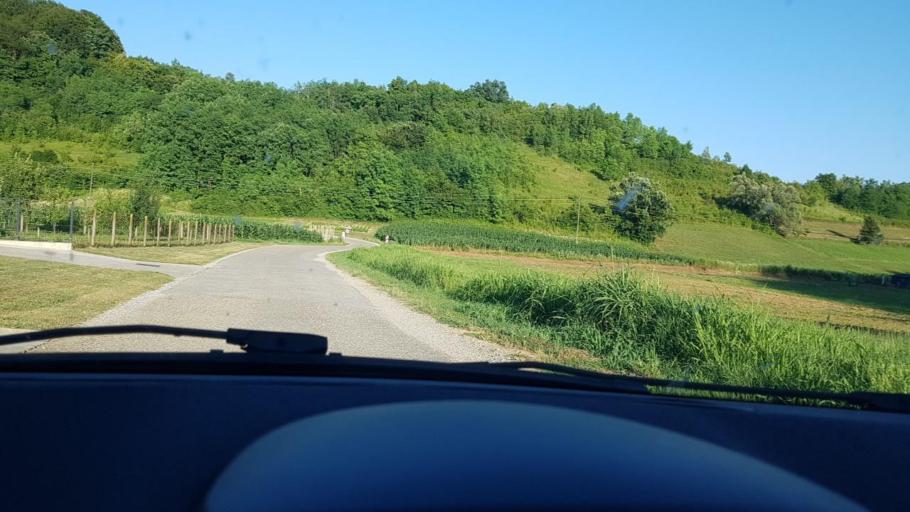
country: HR
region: Krapinsko-Zagorska
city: Mihovljan
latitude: 46.0915
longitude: 15.9367
